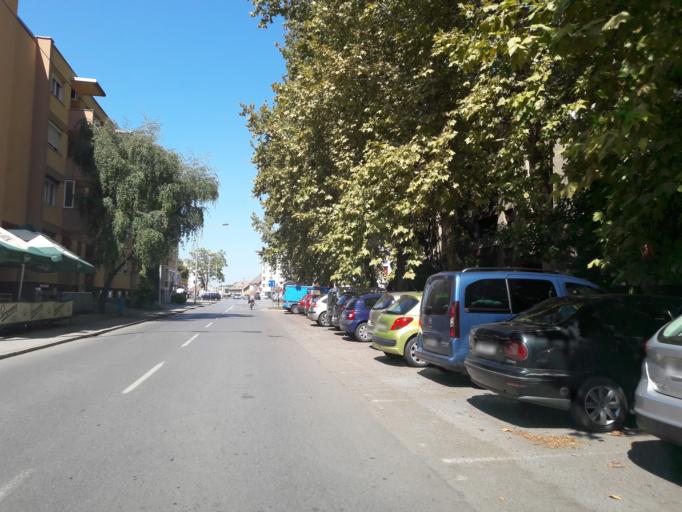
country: HR
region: Osjecko-Baranjska
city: Visnjevac
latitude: 45.5628
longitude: 18.6532
